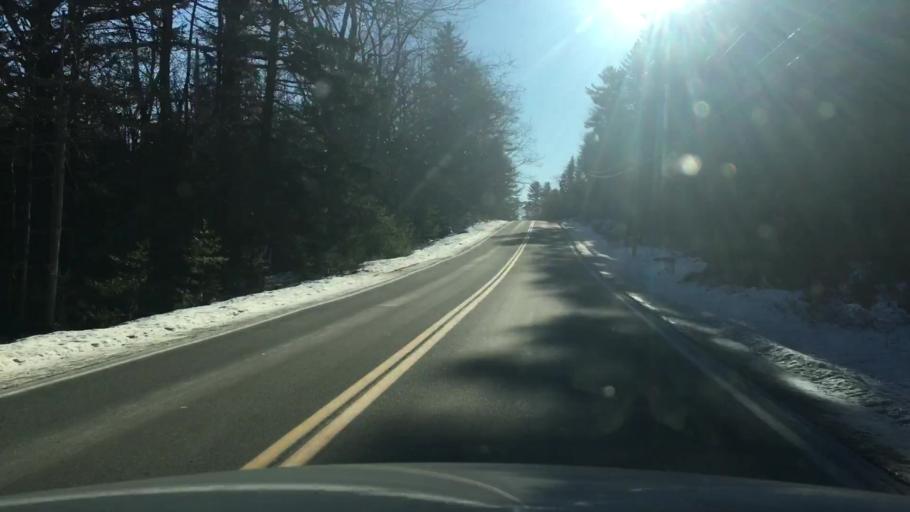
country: US
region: Maine
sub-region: Hancock County
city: Orland
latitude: 44.5163
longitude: -68.7513
